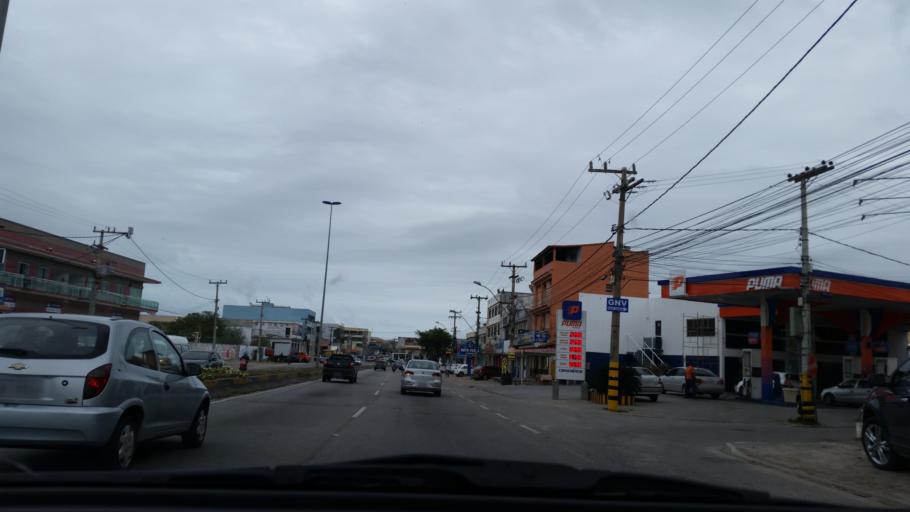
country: BR
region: Rio de Janeiro
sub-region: Sao Pedro Da Aldeia
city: Sao Pedro da Aldeia
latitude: -22.8333
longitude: -42.0980
